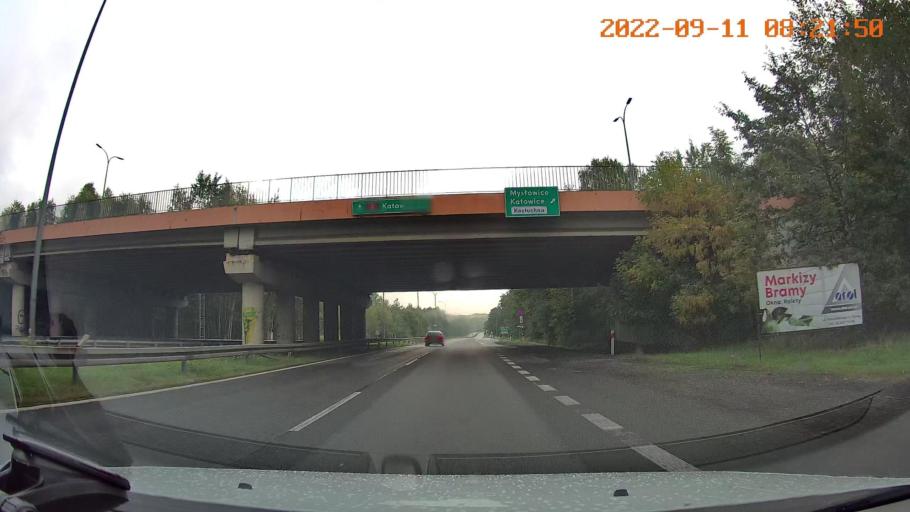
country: PL
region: Silesian Voivodeship
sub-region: Katowice
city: Murcki
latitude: 50.1705
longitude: 19.0198
